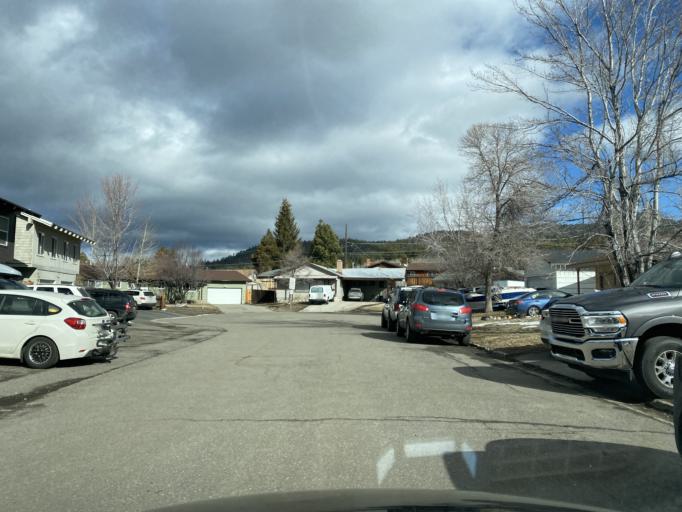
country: US
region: Nevada
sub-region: Douglas County
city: Kingsbury
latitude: 38.9703
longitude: -119.9380
